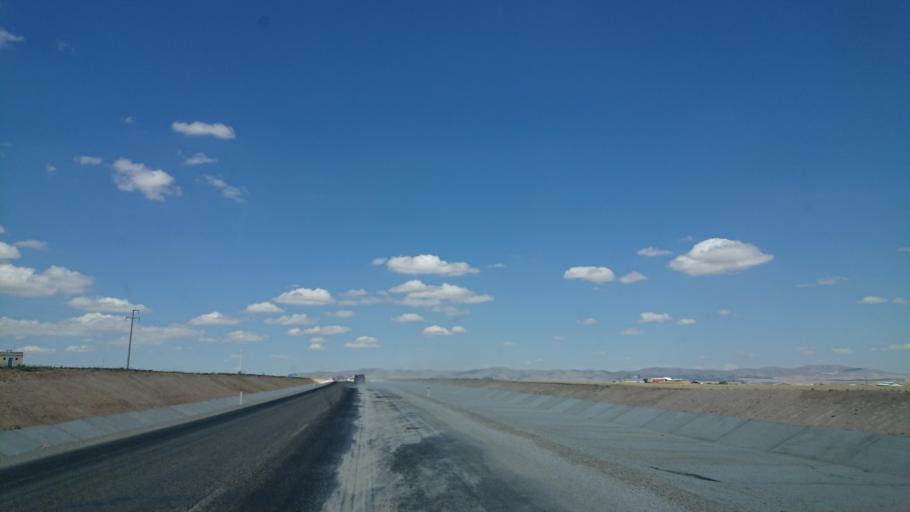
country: TR
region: Kirsehir
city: Kirsehir
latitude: 39.1273
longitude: 34.0341
